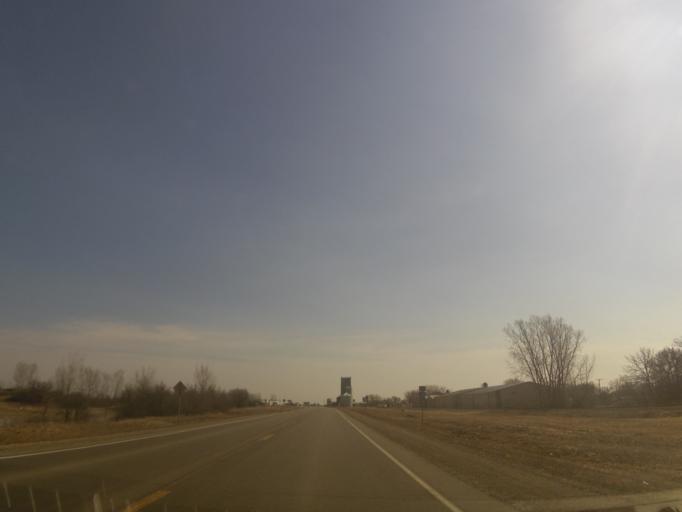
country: US
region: North Dakota
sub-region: Grand Forks County
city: Grand Forks
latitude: 48.0812
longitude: -97.1795
